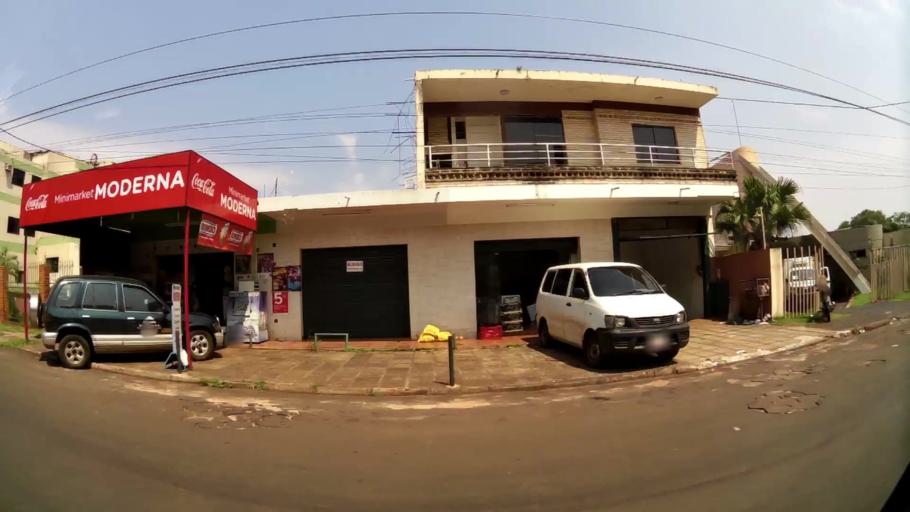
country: PY
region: Alto Parana
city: Presidente Franco
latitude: -25.5224
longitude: -54.6224
